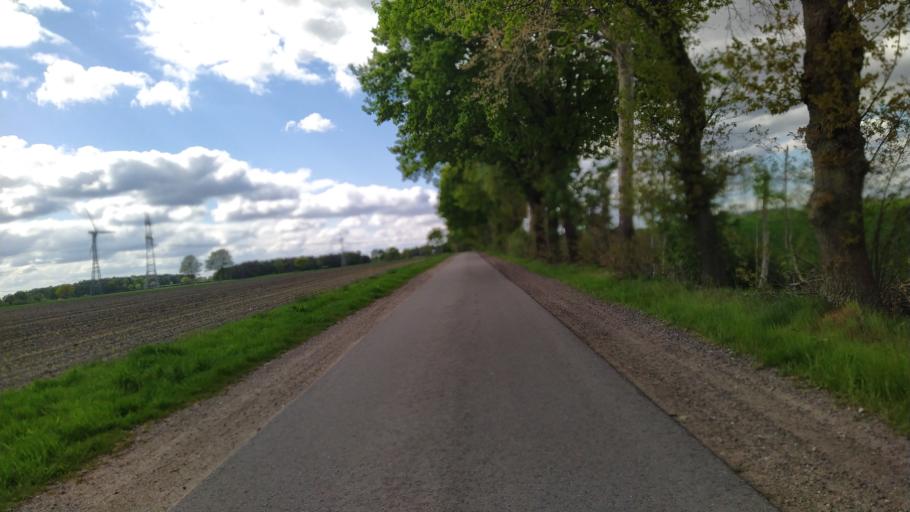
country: DE
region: Lower Saxony
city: Brest
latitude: 53.4399
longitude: 9.4067
